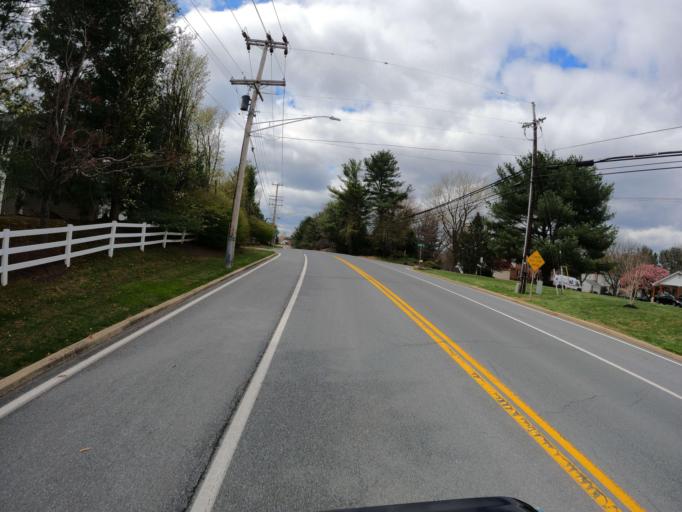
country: US
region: Maryland
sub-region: Howard County
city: North Laurel
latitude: 39.1412
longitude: -76.8870
